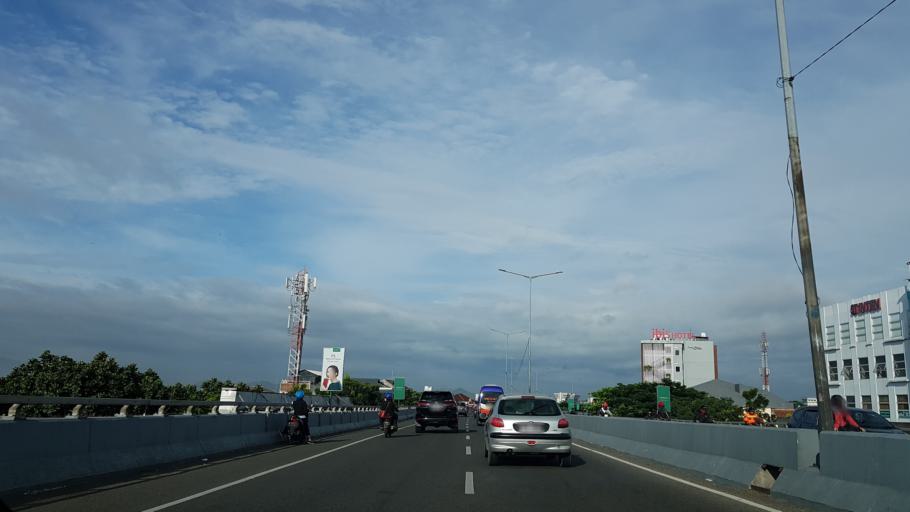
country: ID
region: West Java
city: Bandung
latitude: -6.9003
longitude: 107.5979
